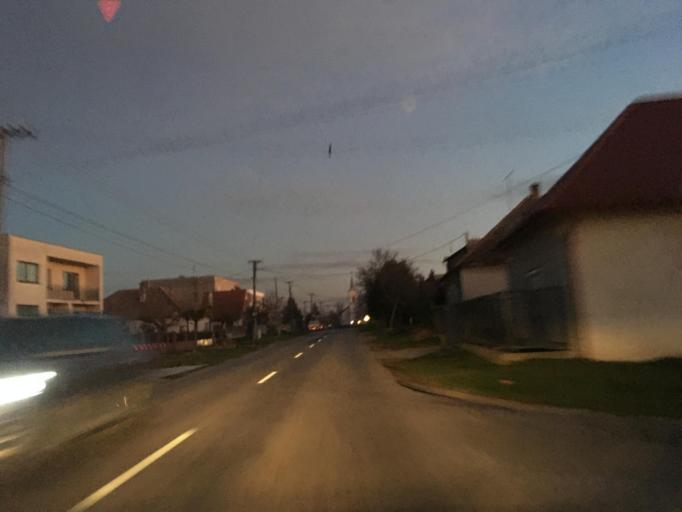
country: SK
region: Nitriansky
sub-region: Okres Komarno
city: Hurbanovo
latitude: 47.9018
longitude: 18.1387
